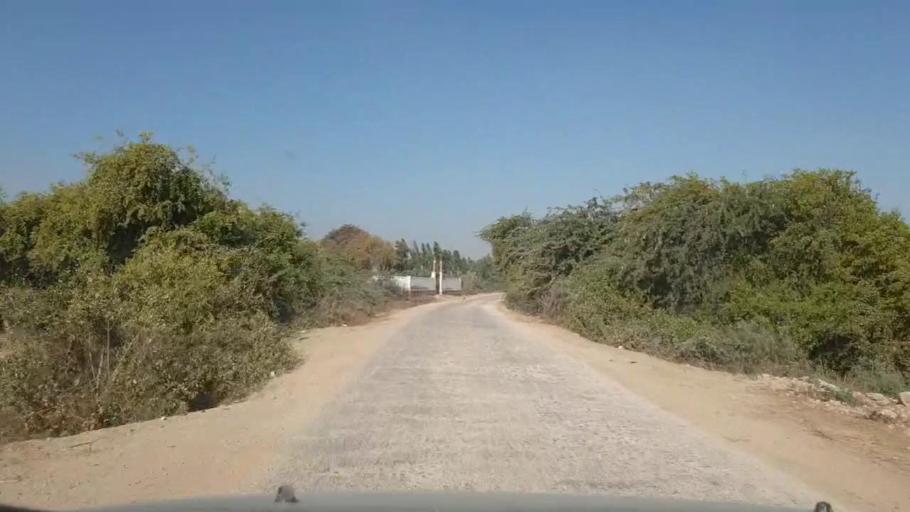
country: PK
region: Sindh
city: Thatta
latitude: 24.7921
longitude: 67.9026
